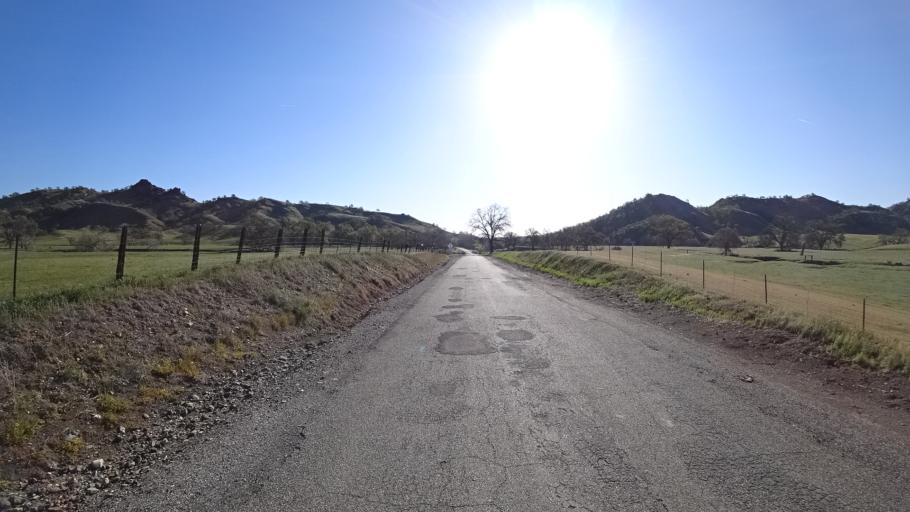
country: US
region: California
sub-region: Tehama County
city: Rancho Tehama Reserve
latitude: 39.7936
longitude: -122.5362
